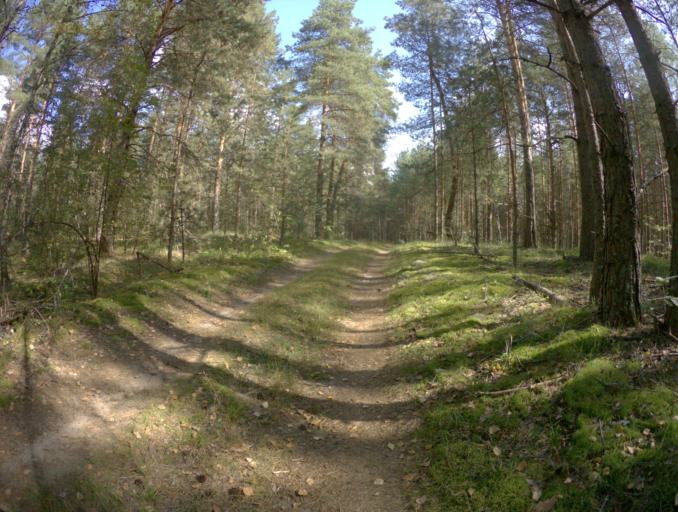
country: RU
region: Vladimir
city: Pokrov
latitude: 55.8505
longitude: 39.2634
